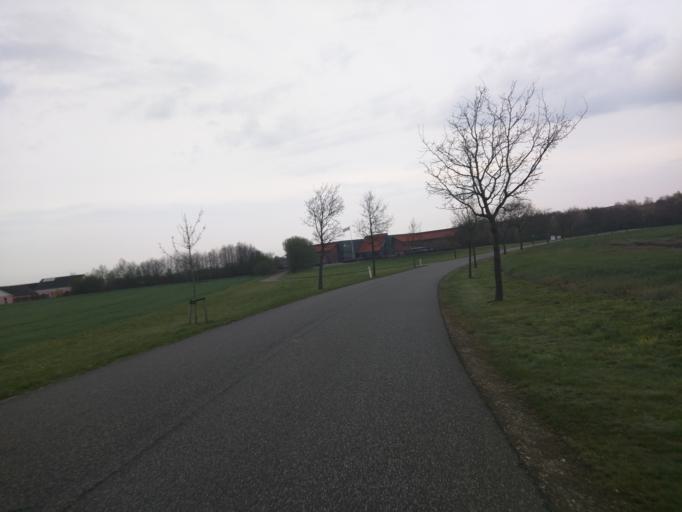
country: DK
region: Central Jutland
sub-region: Viborg Kommune
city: Bjerringbro
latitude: 56.4837
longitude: 9.5775
